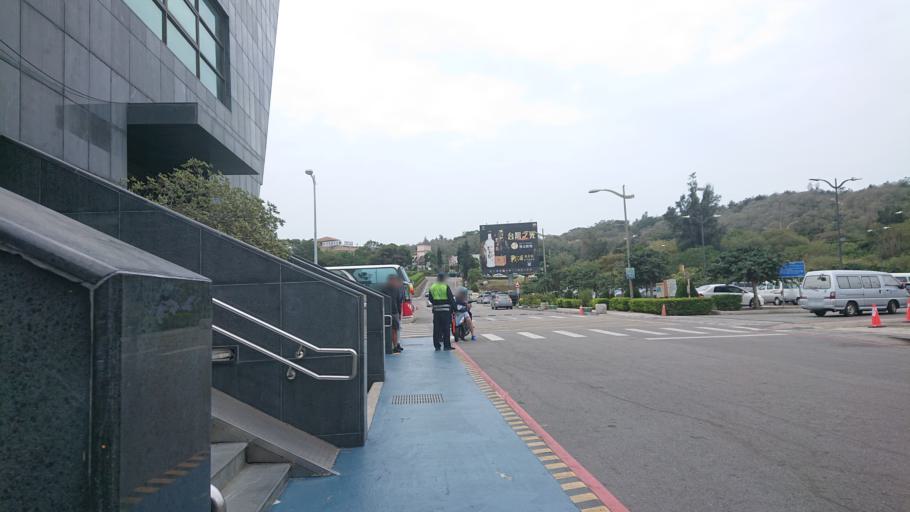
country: TW
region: Fukien
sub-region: Kinmen
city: Jincheng
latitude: 24.4152
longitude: 118.2866
